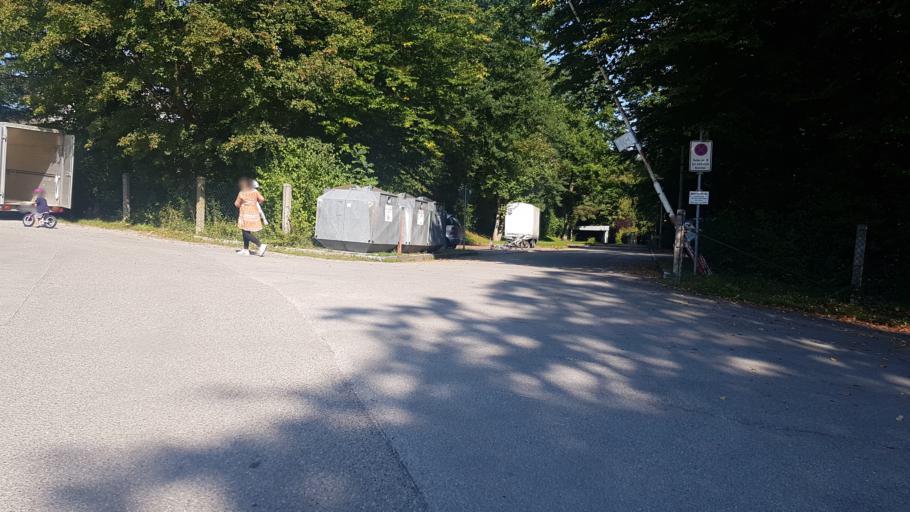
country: DE
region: Bavaria
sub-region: Upper Bavaria
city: Herrsching am Ammersee
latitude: 48.0117
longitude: 11.1631
